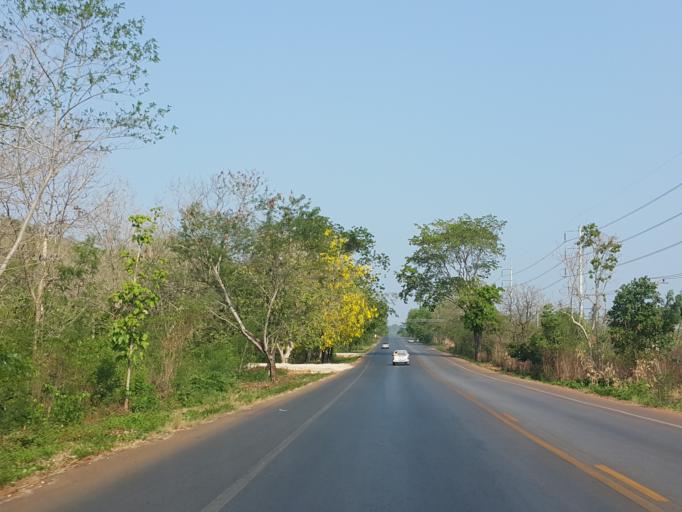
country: TH
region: Kanchanaburi
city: Sai Yok
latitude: 14.1045
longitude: 99.2225
